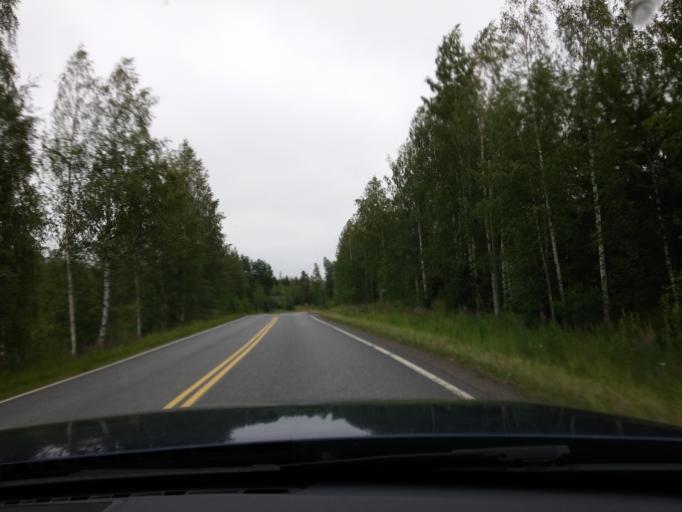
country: FI
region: Central Finland
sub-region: Joutsa
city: Joutsa
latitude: 61.7995
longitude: 25.9959
